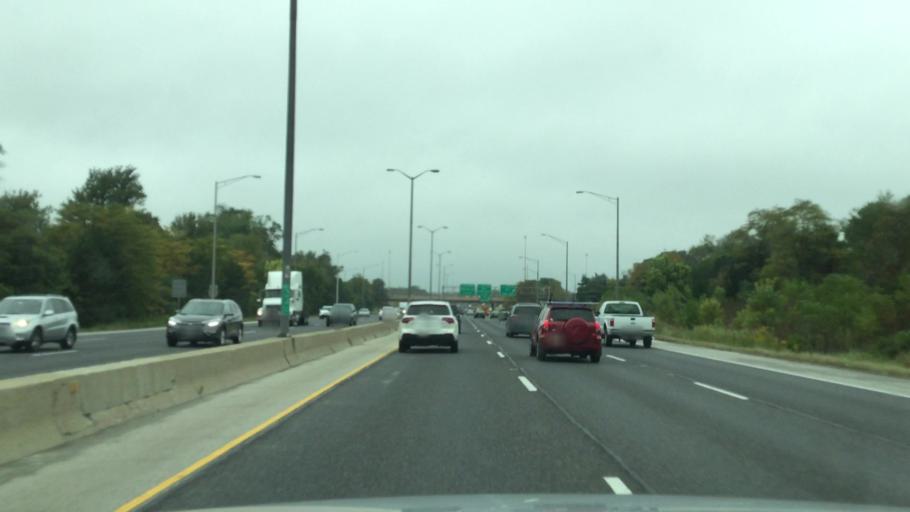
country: US
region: Illinois
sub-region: Cook County
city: Glenview
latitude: 42.0760
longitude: -87.7586
